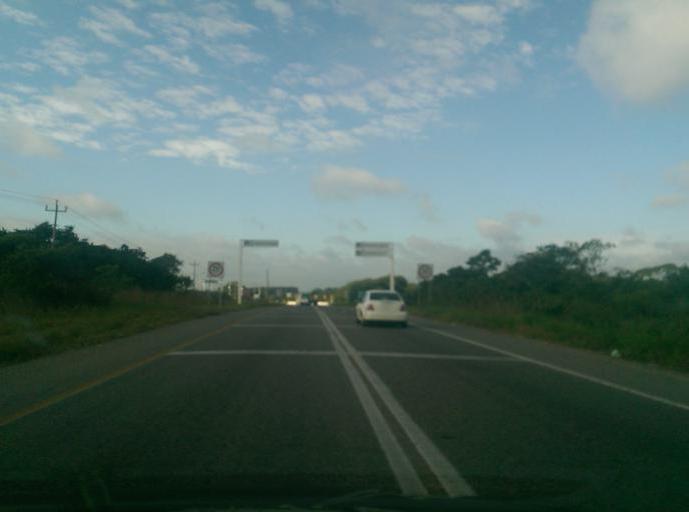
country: MX
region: Chiapas
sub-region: Catazaja
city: Catazaja
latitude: 17.7100
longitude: -92.0175
